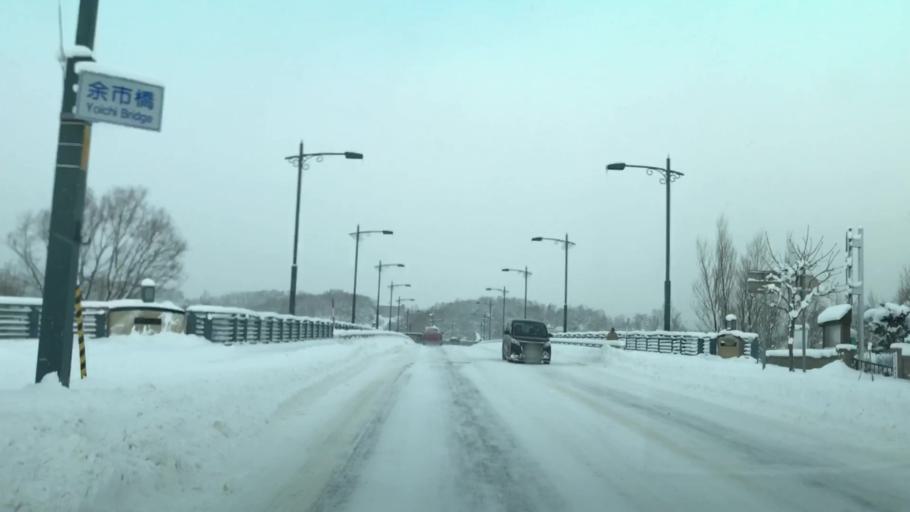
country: JP
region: Hokkaido
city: Yoichi
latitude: 43.1903
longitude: 140.7884
